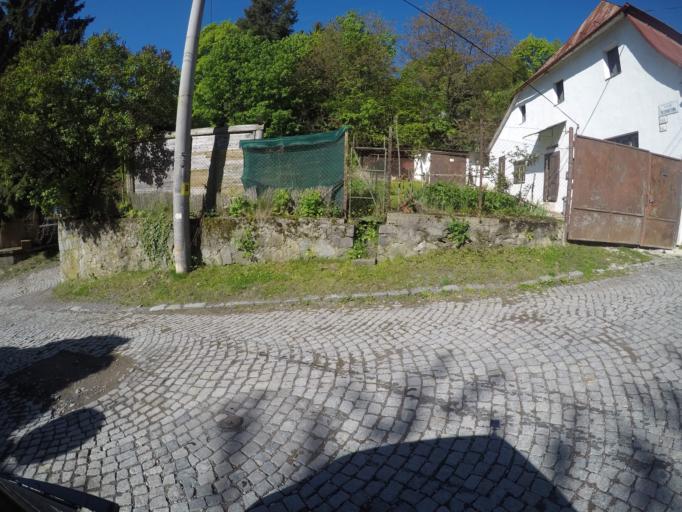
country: SK
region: Banskobystricky
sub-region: Okres Banska Bystrica
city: Banska Stiavnica
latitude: 48.4620
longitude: 18.8915
